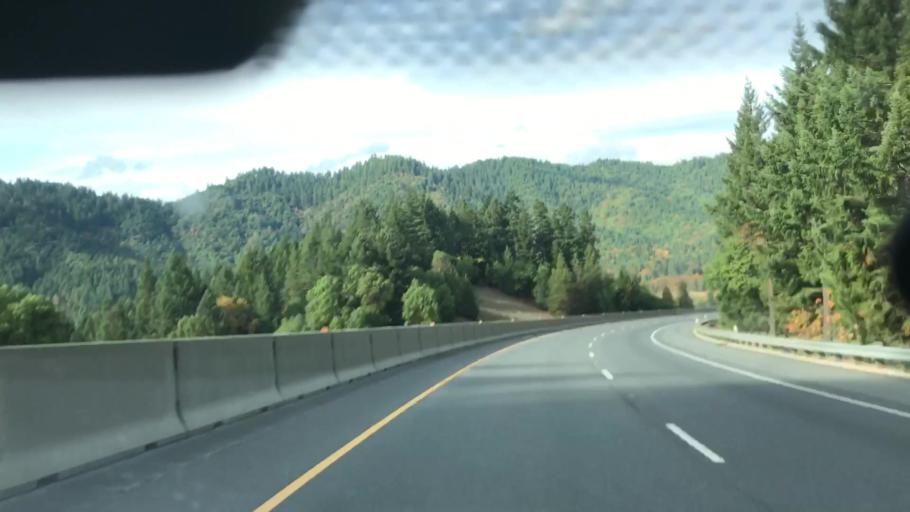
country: US
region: Oregon
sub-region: Douglas County
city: Canyonville
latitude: 42.7419
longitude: -123.3727
